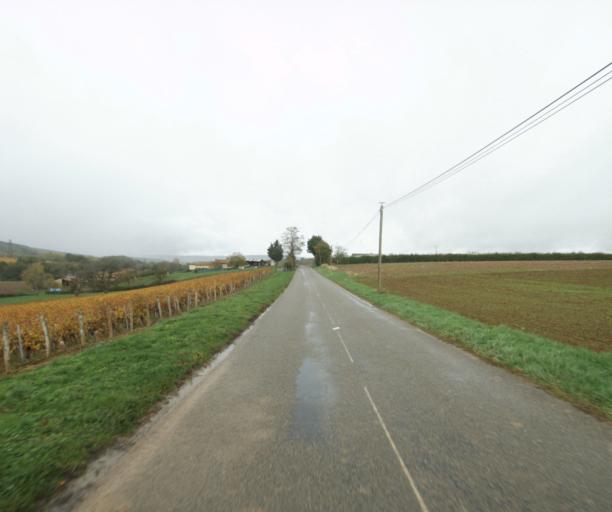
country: FR
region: Rhone-Alpes
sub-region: Departement de l'Ain
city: Pont-de-Vaux
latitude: 46.4771
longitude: 4.8644
